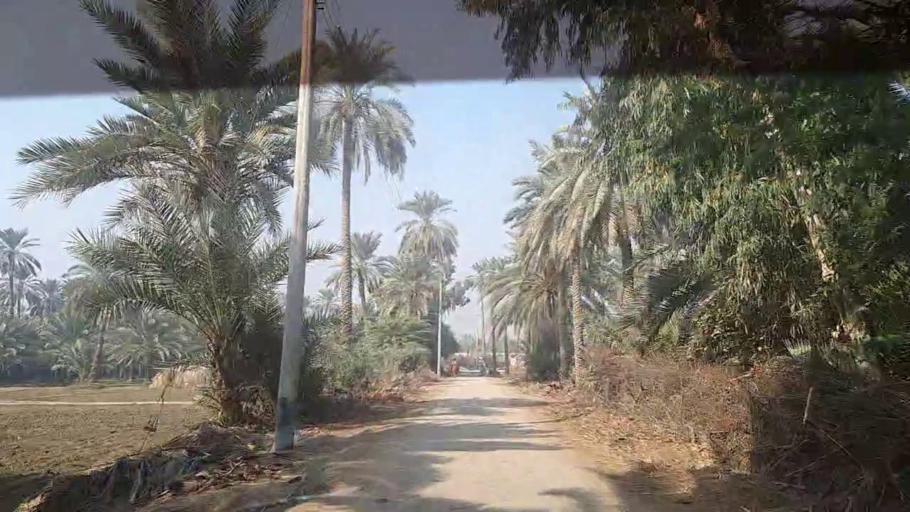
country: PK
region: Sindh
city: Khairpur
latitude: 27.4683
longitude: 68.7142
